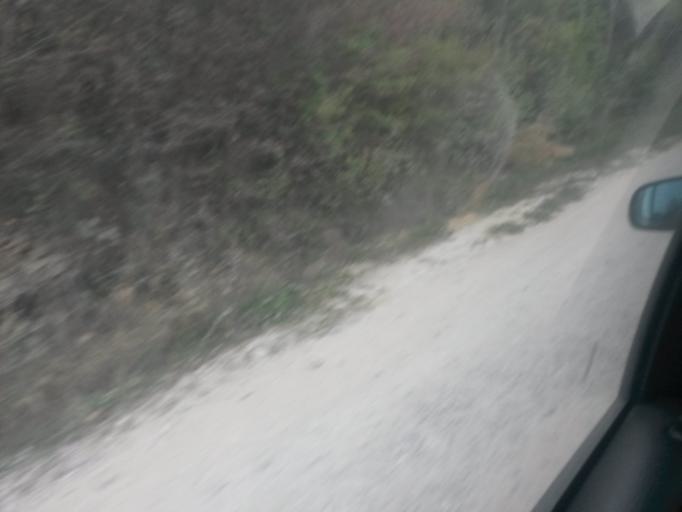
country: RO
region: Alba
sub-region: Comuna Livezile
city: Livezile
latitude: 46.3191
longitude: 23.6005
